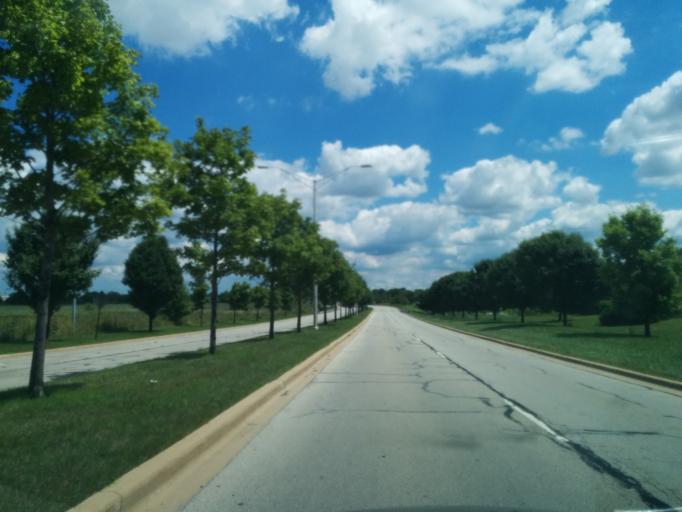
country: US
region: Illinois
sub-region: Will County
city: Romeoville
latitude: 41.6755
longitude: -88.1155
